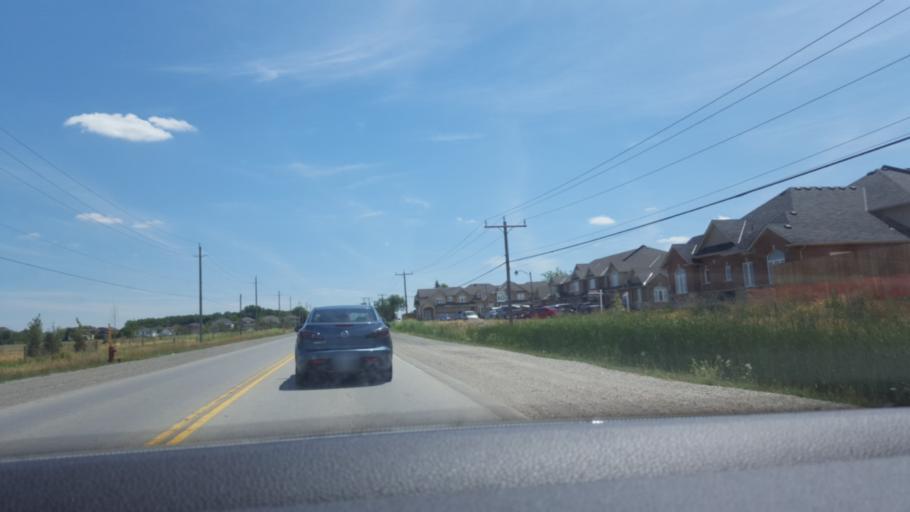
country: CA
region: Ontario
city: Hamilton
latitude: 43.1787
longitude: -79.8007
